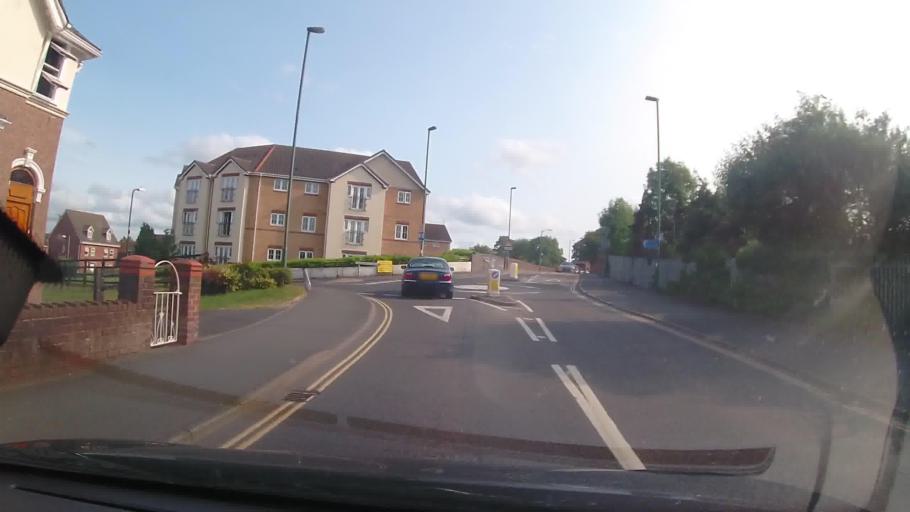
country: GB
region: England
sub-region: Shropshire
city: Shrewsbury
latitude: 52.7180
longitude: -2.7517
